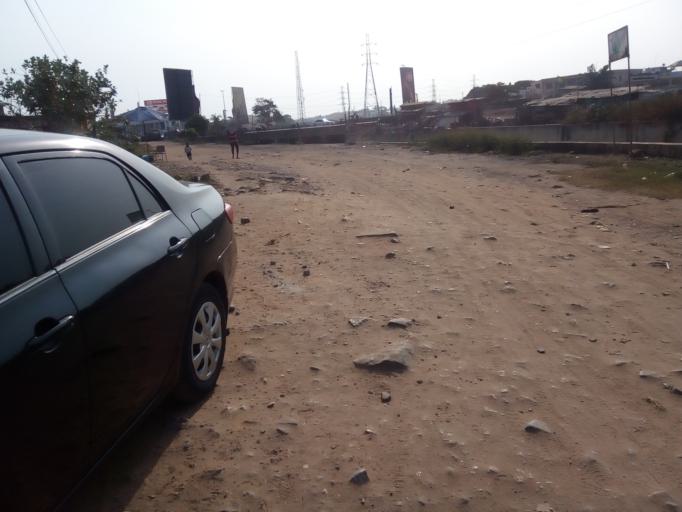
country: GH
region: Greater Accra
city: Accra
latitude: 5.5863
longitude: -0.2164
